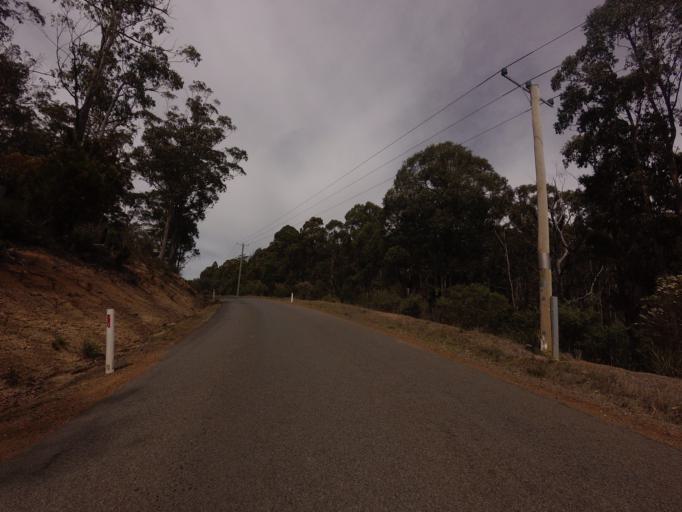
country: AU
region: Tasmania
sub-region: Sorell
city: Sorell
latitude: -42.5817
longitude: 147.5579
